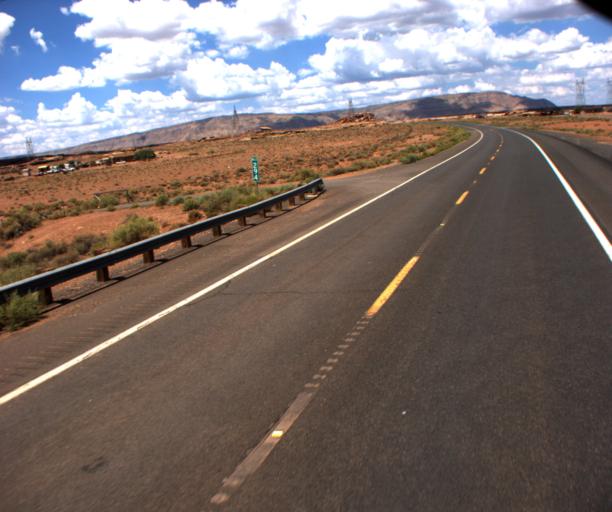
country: US
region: Arizona
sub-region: Coconino County
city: Tuba City
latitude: 35.8578
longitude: -111.4452
